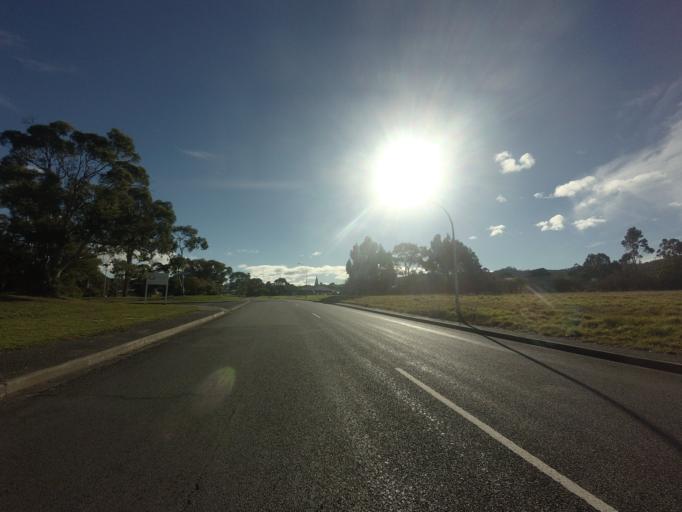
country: AU
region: Tasmania
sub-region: Clarence
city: Rokeby
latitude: -42.8960
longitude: 147.4465
